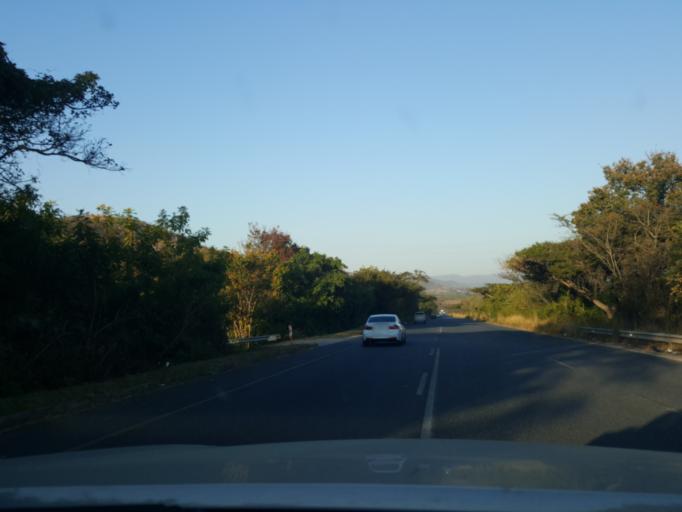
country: ZA
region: Mpumalanga
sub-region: Ehlanzeni District
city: Nelspruit
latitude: -25.4549
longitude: 31.0445
